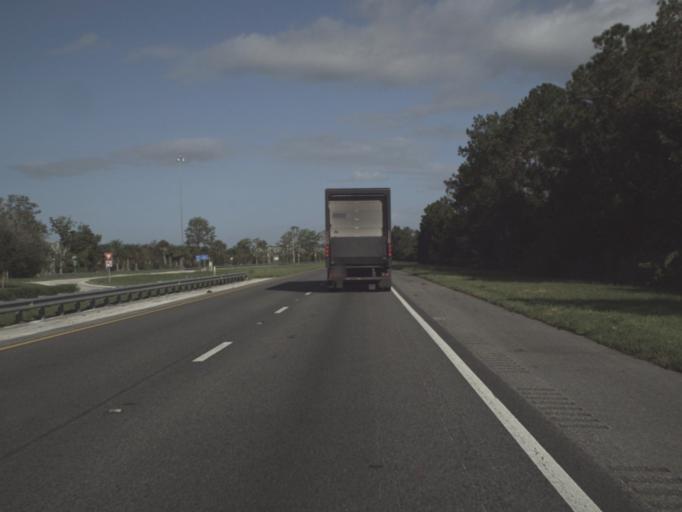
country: US
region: Florida
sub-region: Osceola County
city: Saint Cloud
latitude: 28.0953
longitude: -81.2734
